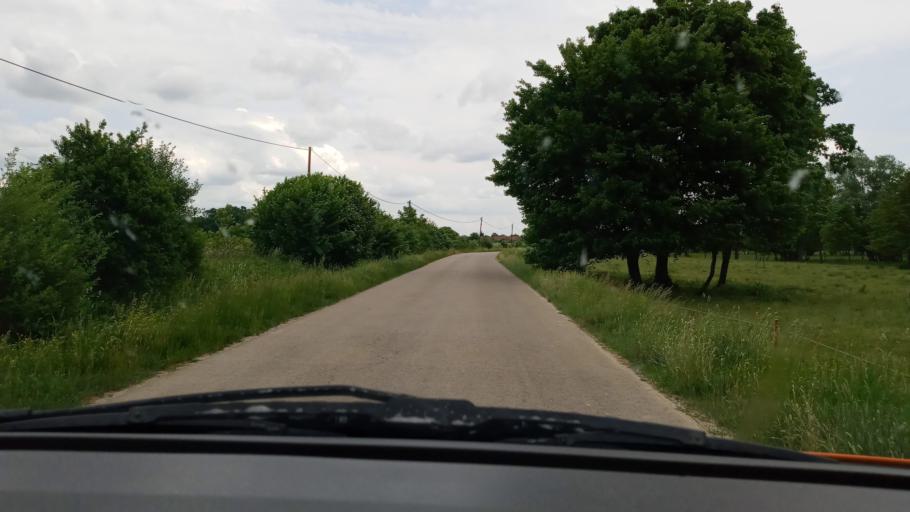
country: HU
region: Baranya
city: Vajszlo
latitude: 45.8286
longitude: 17.9828
